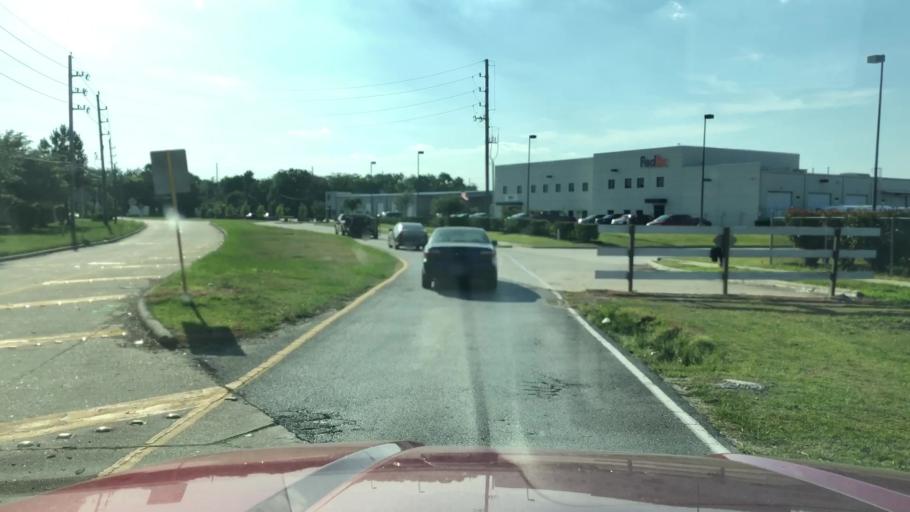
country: US
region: Texas
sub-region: Harris County
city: Hudson
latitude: 29.9461
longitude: -95.4955
